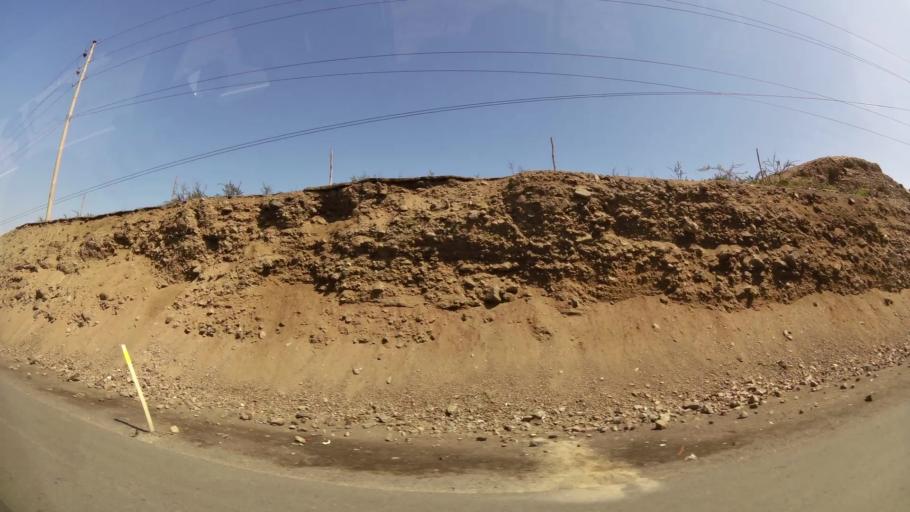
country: PE
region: Lima
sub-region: Provincia de Canete
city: Quilmana
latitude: -12.9370
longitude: -76.4973
